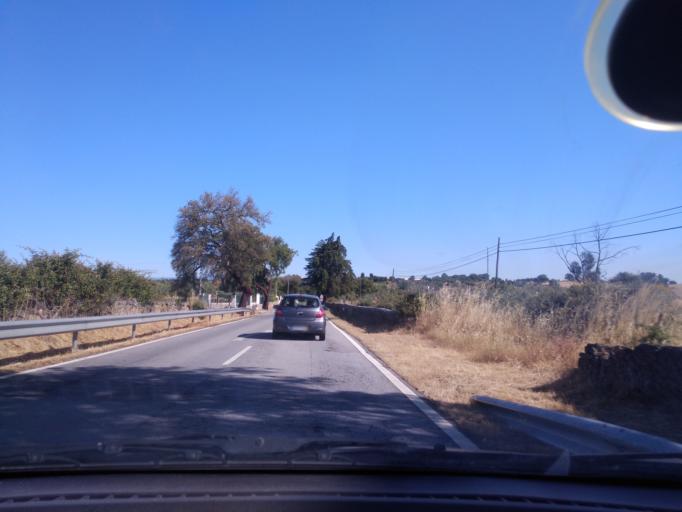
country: PT
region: Portalegre
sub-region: Nisa
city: Nisa
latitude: 39.4966
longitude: -7.6423
